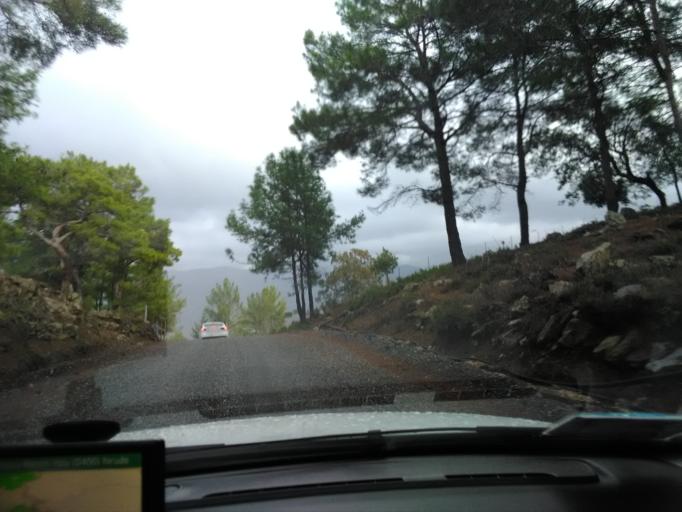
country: TR
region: Antalya
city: Gazipasa
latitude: 36.1578
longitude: 32.4304
